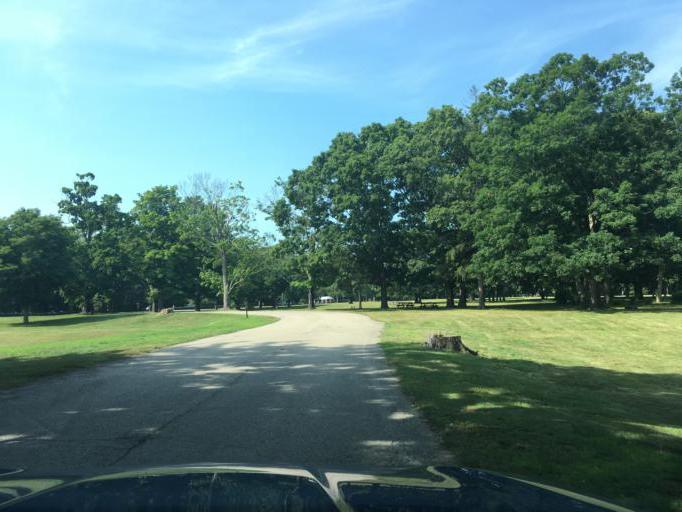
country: US
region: Rhode Island
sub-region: Kent County
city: East Greenwich
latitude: 41.6549
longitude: -71.4389
